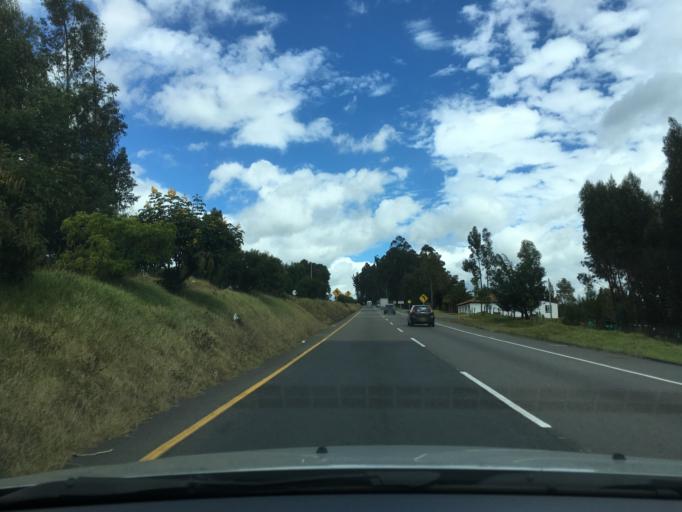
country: CO
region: Boyaca
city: Tuta
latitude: 5.6681
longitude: -73.2700
